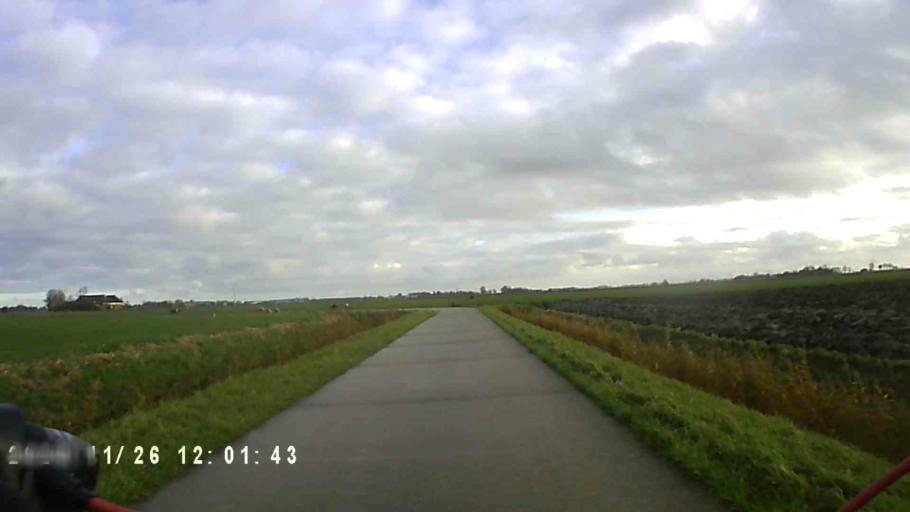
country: NL
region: Groningen
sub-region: Gemeente Bedum
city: Bedum
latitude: 53.3211
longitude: 6.6114
